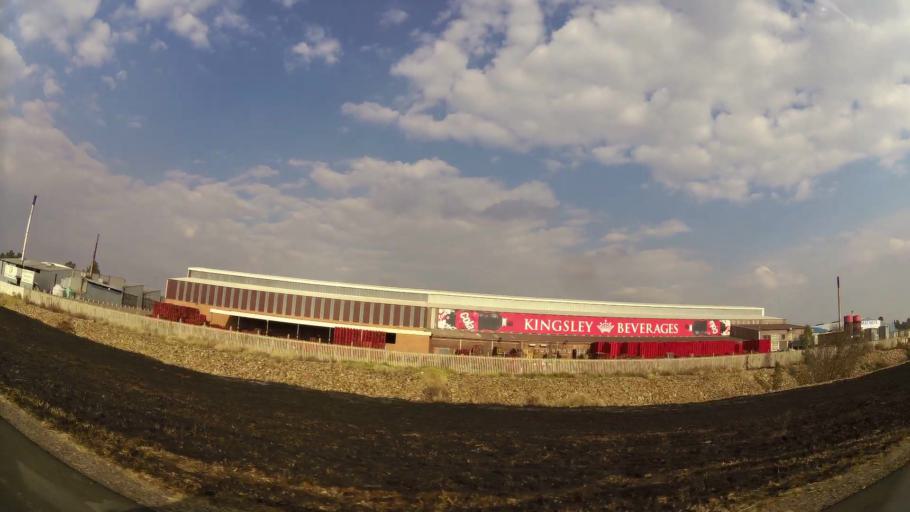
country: ZA
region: Gauteng
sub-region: Ekurhuleni Metropolitan Municipality
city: Springs
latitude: -26.2785
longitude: 28.4553
